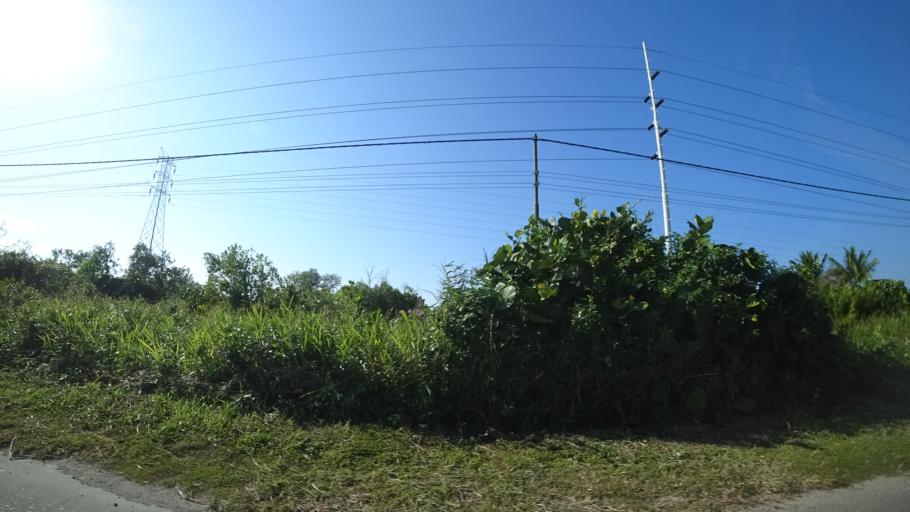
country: BN
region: Tutong
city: Tutong
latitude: 4.7261
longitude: 114.5510
